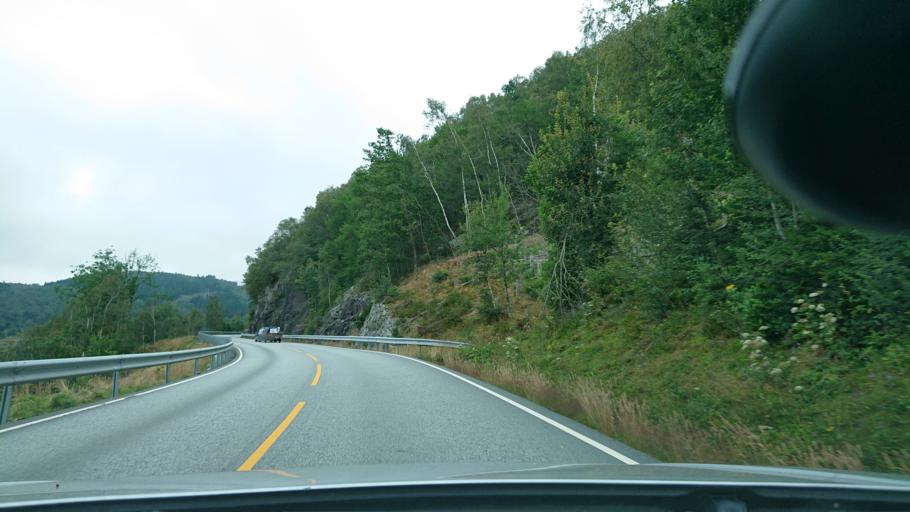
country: NO
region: Rogaland
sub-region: Hjelmeland
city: Hjelmelandsvagen
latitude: 59.1729
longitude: 6.1409
